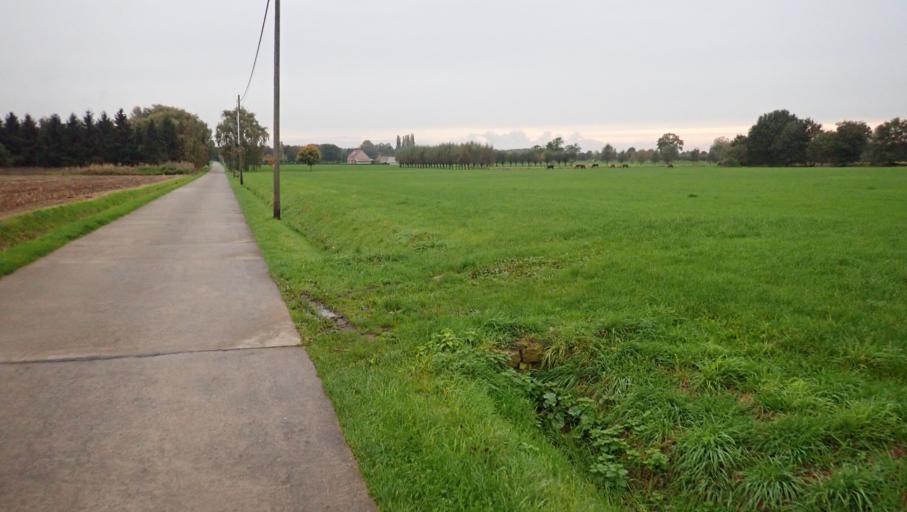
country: BE
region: Flanders
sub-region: Provincie Antwerpen
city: Berlaar
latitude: 51.1112
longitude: 4.6220
